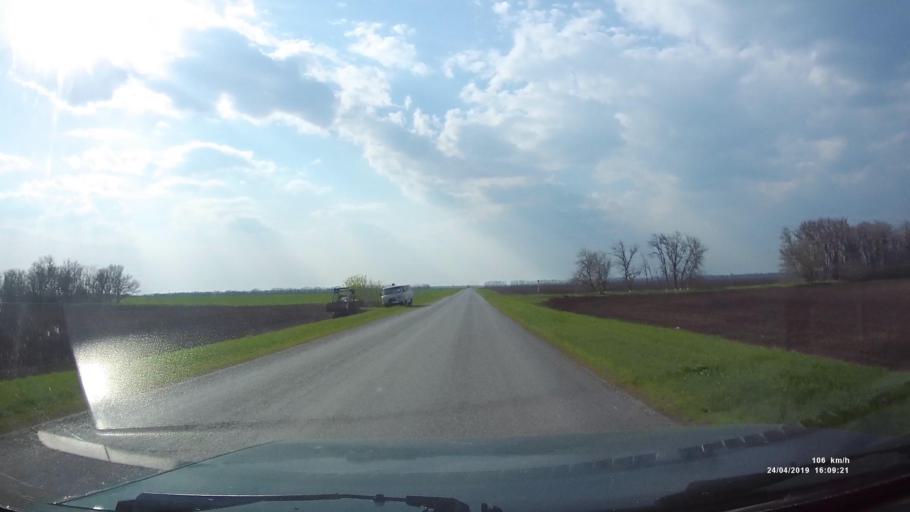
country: RU
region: Rostov
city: Sovetskoye
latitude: 46.7072
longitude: 42.2914
